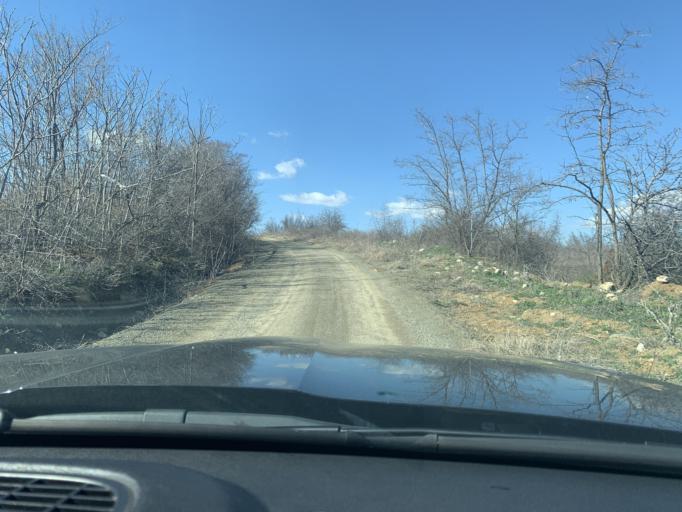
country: MK
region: Demir Kapija
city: Demir Kapija
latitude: 41.4133
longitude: 22.2231
